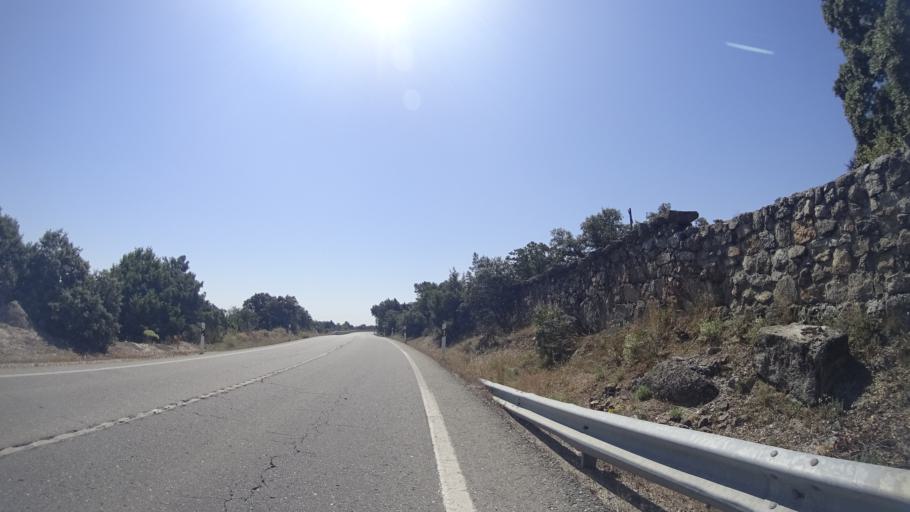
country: ES
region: Madrid
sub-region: Provincia de Madrid
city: Torrelodones
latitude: 40.5935
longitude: -3.9185
